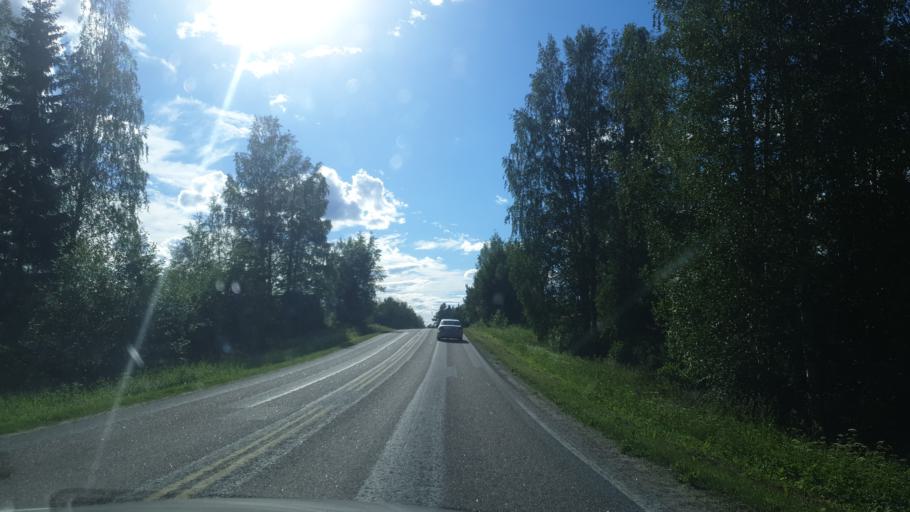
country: FI
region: Southern Savonia
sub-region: Mikkeli
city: Pertunmaa
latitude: 61.5225
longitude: 26.5608
